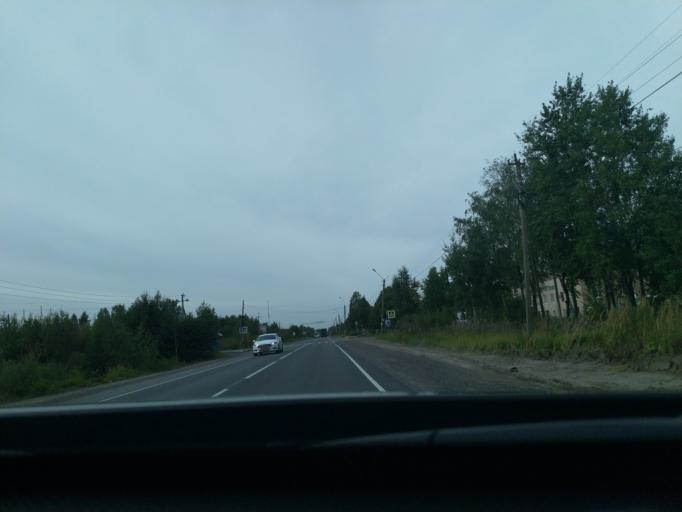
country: RU
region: Leningrad
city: Nikol'skoye
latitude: 59.7221
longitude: 30.7785
